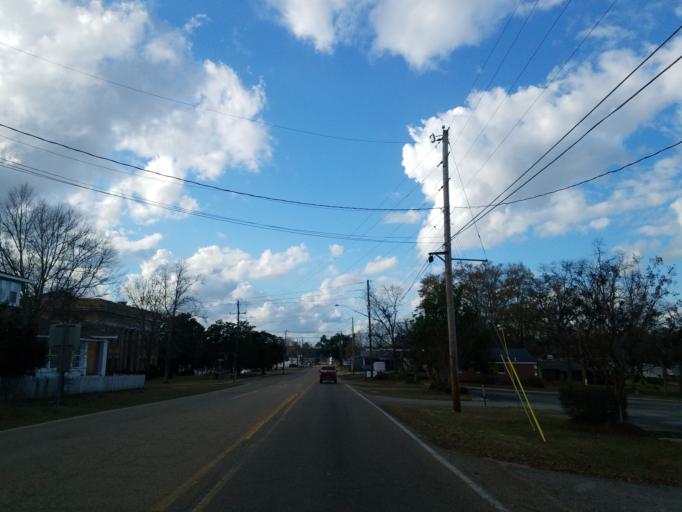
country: US
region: Mississippi
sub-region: Jones County
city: Ellisville
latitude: 31.6041
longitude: -89.1939
